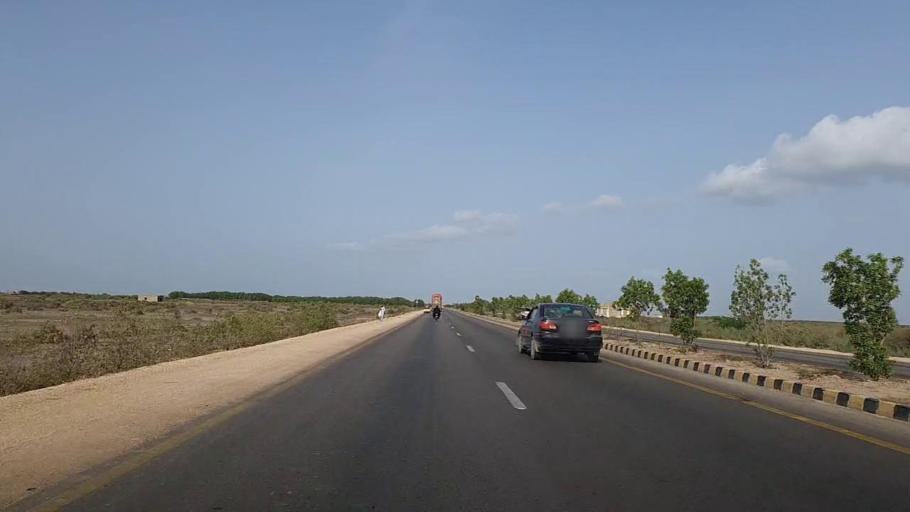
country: PK
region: Sindh
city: Gharo
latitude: 24.7372
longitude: 67.7171
